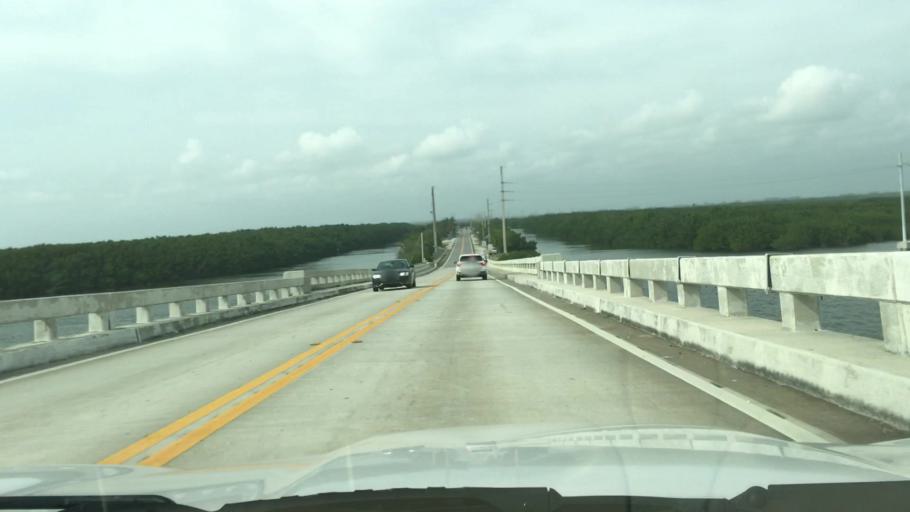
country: US
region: Florida
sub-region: Monroe County
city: North Key Largo
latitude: 25.2883
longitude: -80.3709
